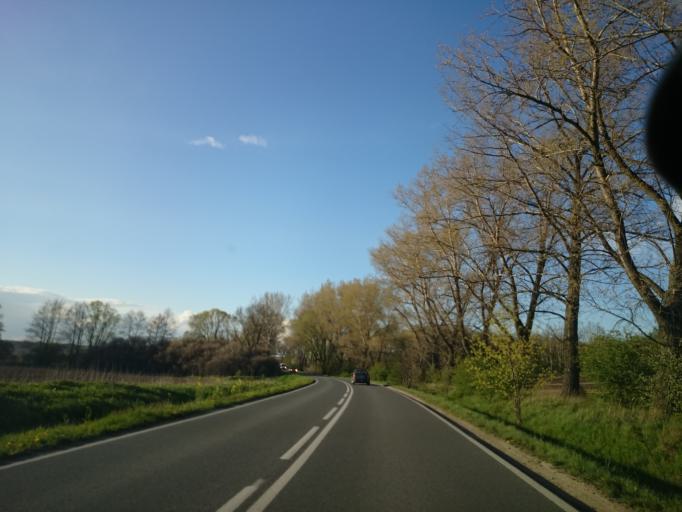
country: PL
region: Lower Silesian Voivodeship
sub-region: Powiat zabkowicki
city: Kamieniec Zabkowicki
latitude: 50.5392
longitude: 16.8647
